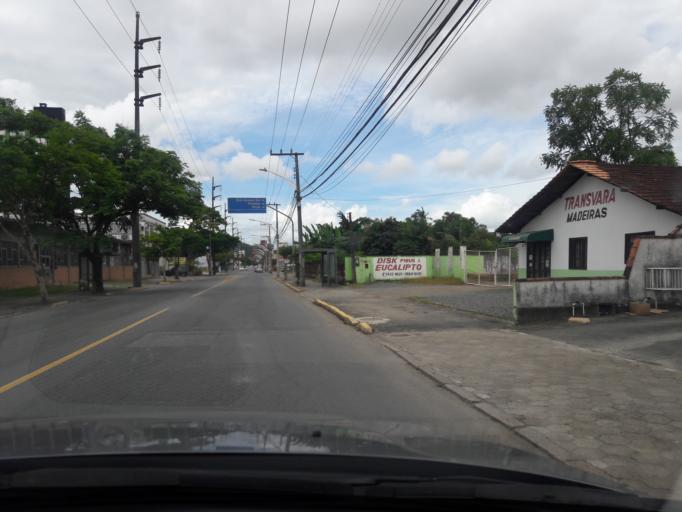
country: BR
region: Santa Catarina
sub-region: Joinville
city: Joinville
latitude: -26.3231
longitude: -48.8541
